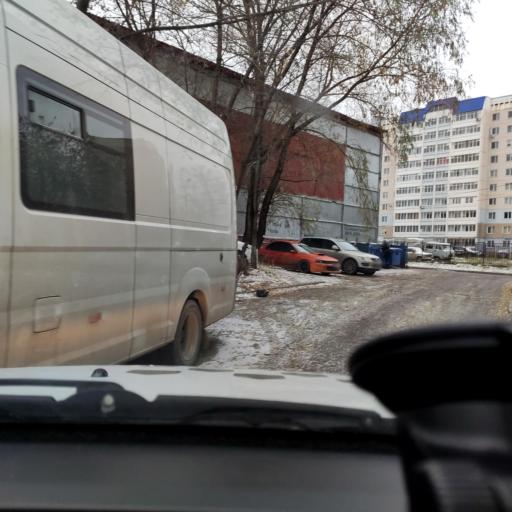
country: RU
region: Perm
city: Perm
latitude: 58.0226
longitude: 56.2732
